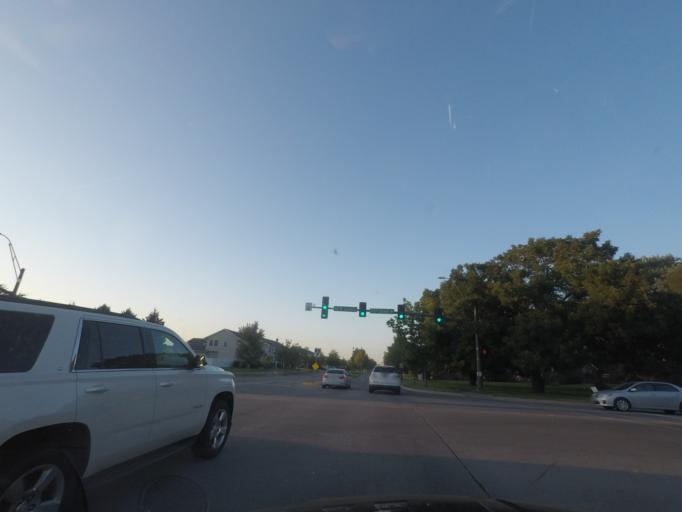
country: US
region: Iowa
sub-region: Story County
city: Ames
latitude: 42.0453
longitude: -93.6448
